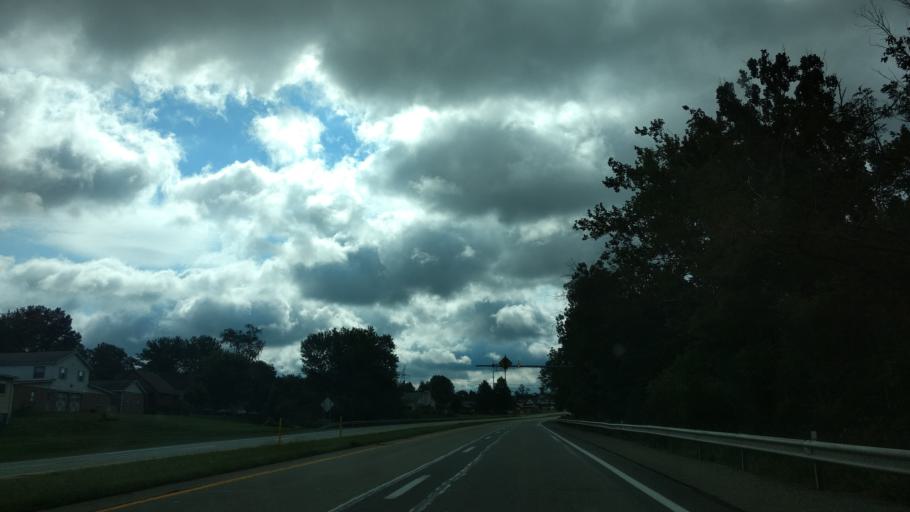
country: US
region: Pennsylvania
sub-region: Westmoreland County
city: Fellsburg
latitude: 40.1611
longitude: -79.7810
